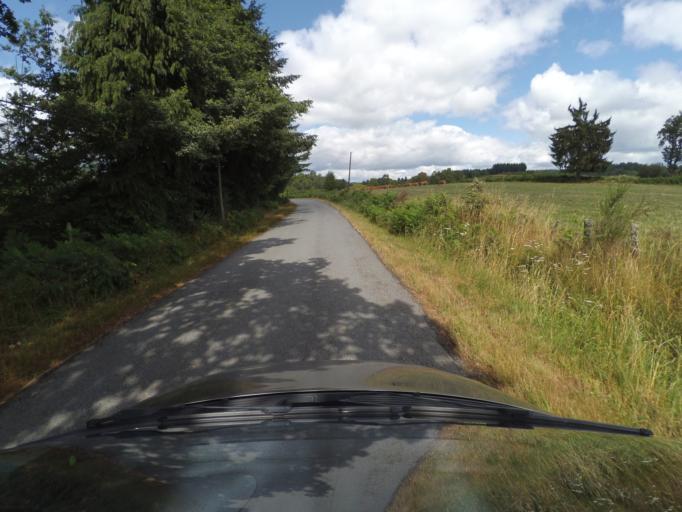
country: FR
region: Limousin
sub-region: Departement de la Creuse
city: Banize
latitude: 45.7819
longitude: 1.9381
